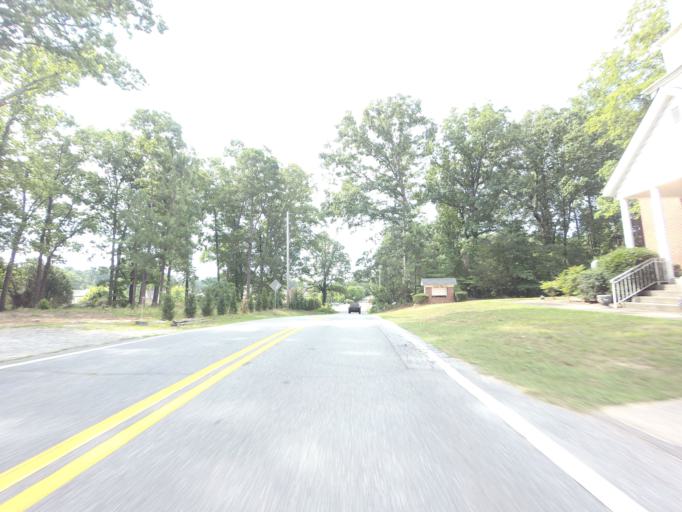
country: US
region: Georgia
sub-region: Gwinnett County
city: Duluth
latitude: 34.0437
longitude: -84.1415
